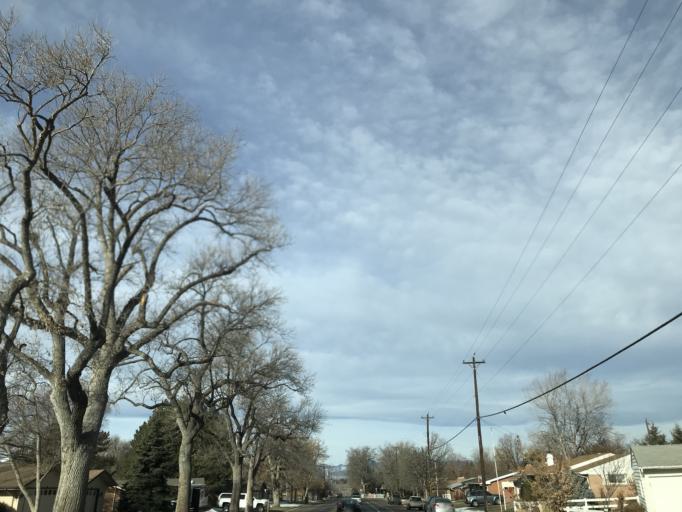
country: US
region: Colorado
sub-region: Arapahoe County
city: Littleton
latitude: 39.5985
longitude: -105.0118
